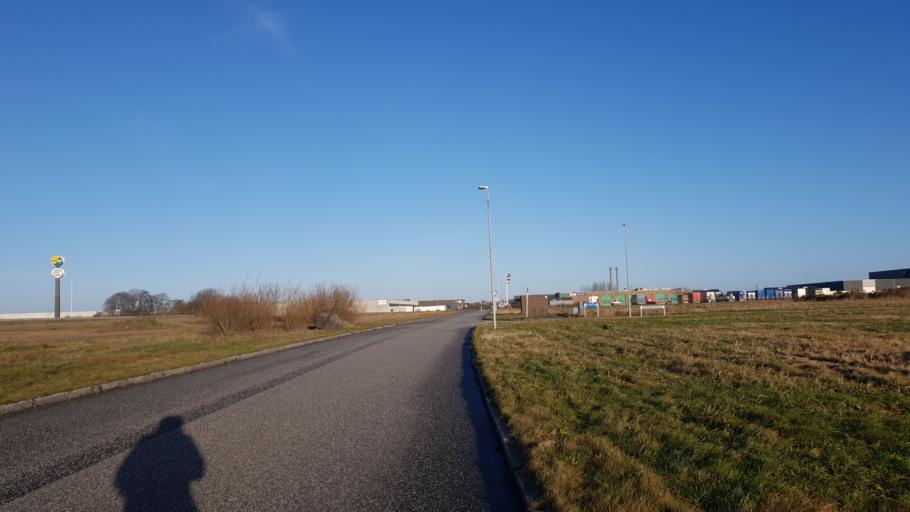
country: DK
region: Central Jutland
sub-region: Hedensted Kommune
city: Hedensted
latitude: 55.7875
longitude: 9.6707
